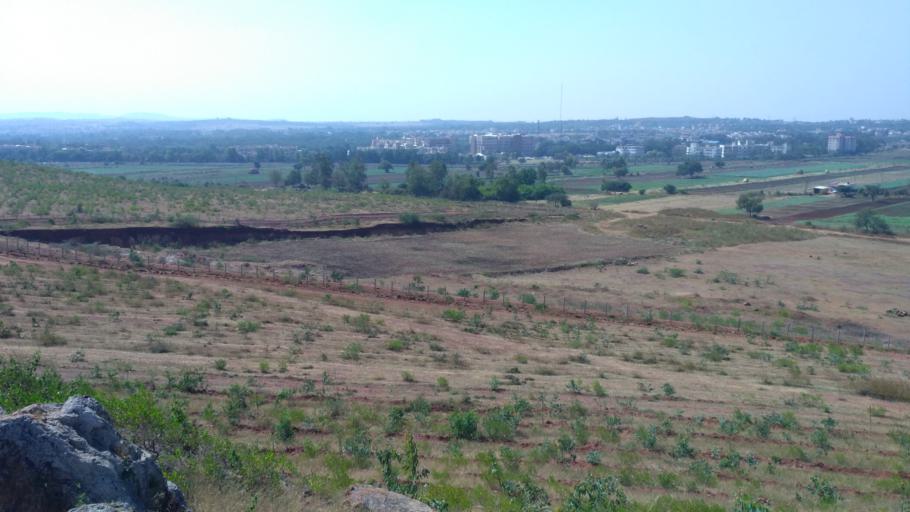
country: IN
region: Karnataka
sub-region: Dharwad
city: Hubli
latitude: 15.4263
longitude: 75.0534
